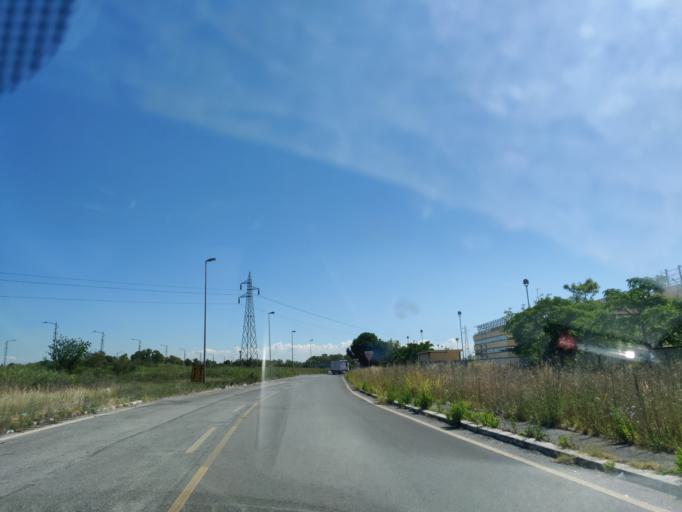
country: IT
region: Latium
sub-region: Citta metropolitana di Roma Capitale
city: Npp 23 (Parco Leonardo)
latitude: 41.8067
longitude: 12.3041
